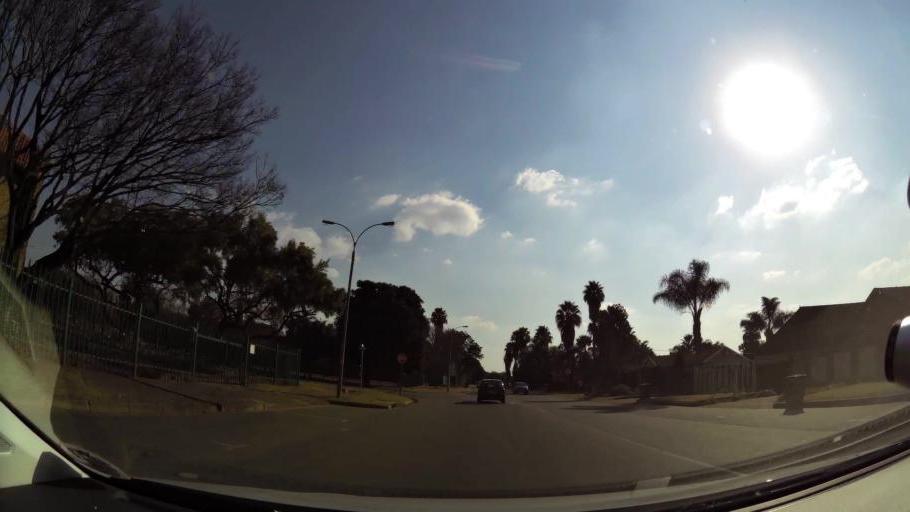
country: ZA
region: Gauteng
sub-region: City of Johannesburg Metropolitan Municipality
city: Modderfontein
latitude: -26.0904
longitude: 28.2023
